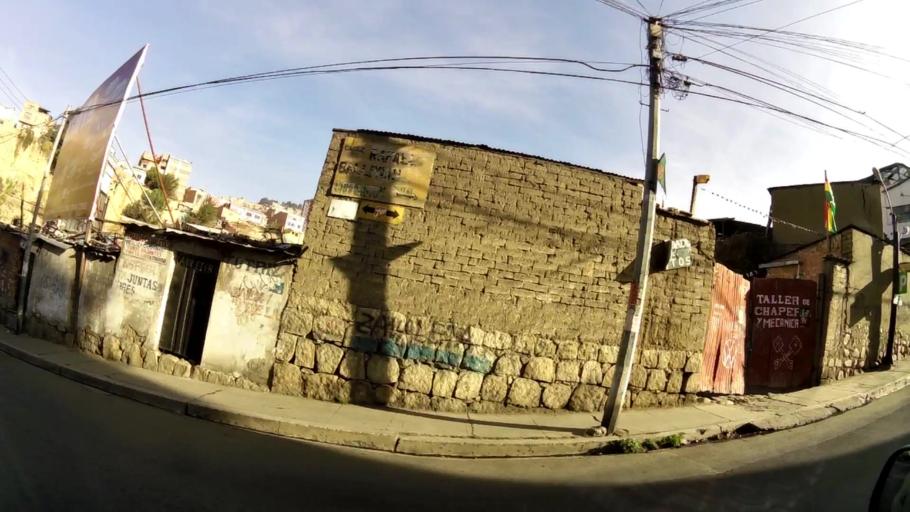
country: BO
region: La Paz
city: La Paz
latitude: -16.4945
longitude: -68.1183
